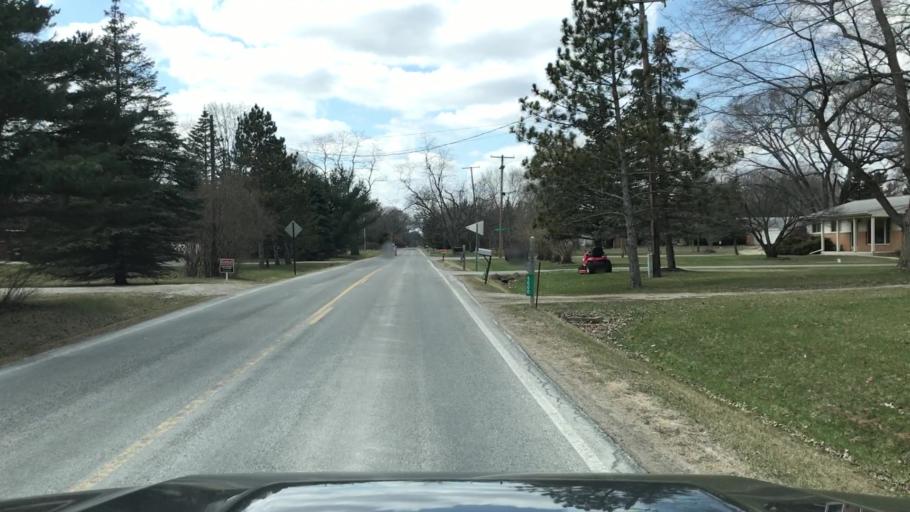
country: US
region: Michigan
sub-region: Washtenaw County
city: Dexter
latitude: 42.2989
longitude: -83.8292
